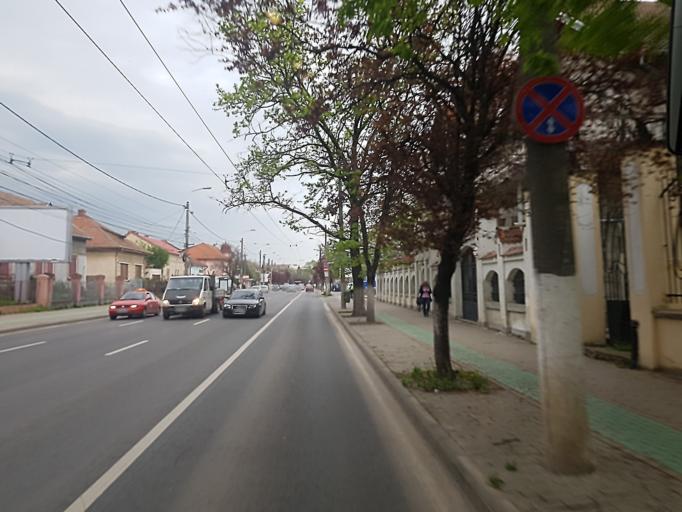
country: RO
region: Timis
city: Timisoara
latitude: 45.7426
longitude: 21.2378
